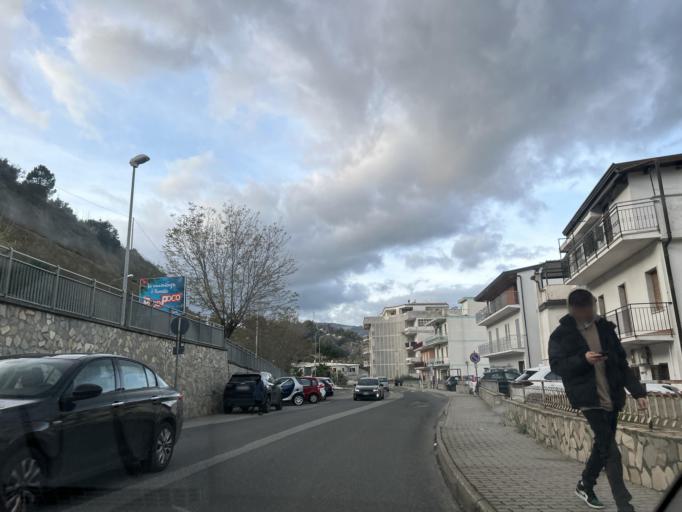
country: IT
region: Calabria
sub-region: Provincia di Catanzaro
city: Soverato Superiore
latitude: 38.6969
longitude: 16.5411
